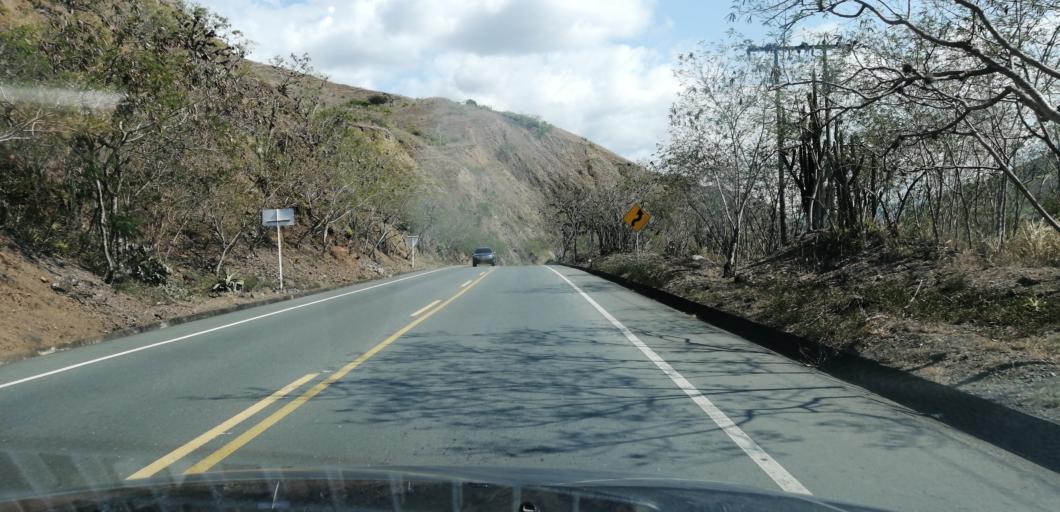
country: CO
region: Valle del Cauca
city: Dagua
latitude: 3.7505
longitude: -76.6615
